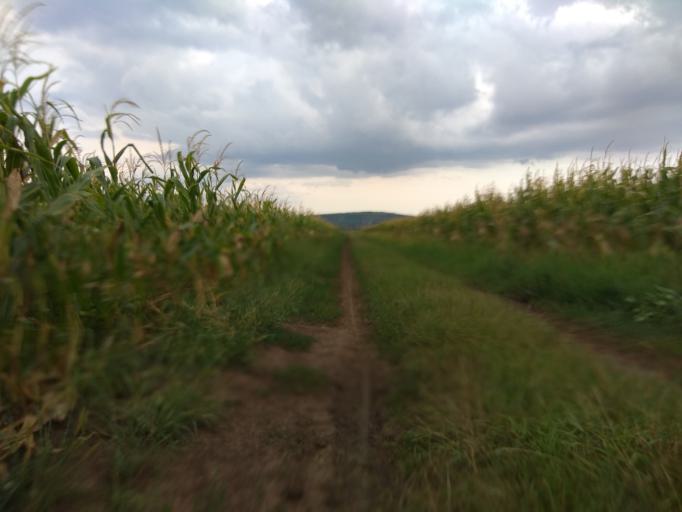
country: HU
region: Borsod-Abauj-Zemplen
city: Bekecs
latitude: 48.1518
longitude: 21.1224
